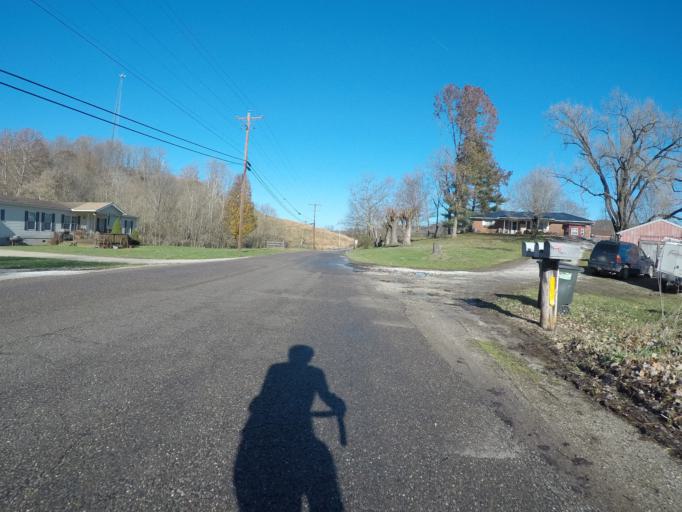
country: US
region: West Virginia
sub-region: Cabell County
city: Huntington
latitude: 38.4809
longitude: -82.4673
